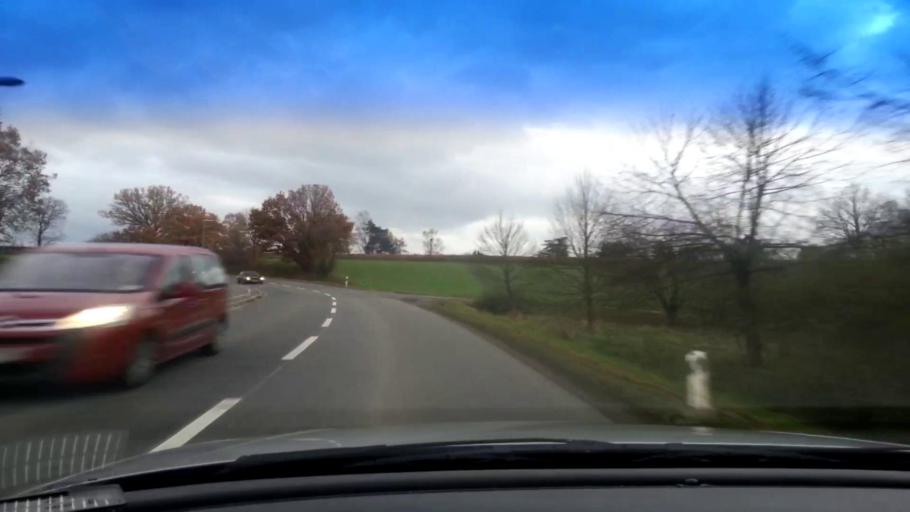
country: DE
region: Bavaria
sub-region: Upper Franconia
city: Stegaurach
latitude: 49.8723
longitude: 10.8665
